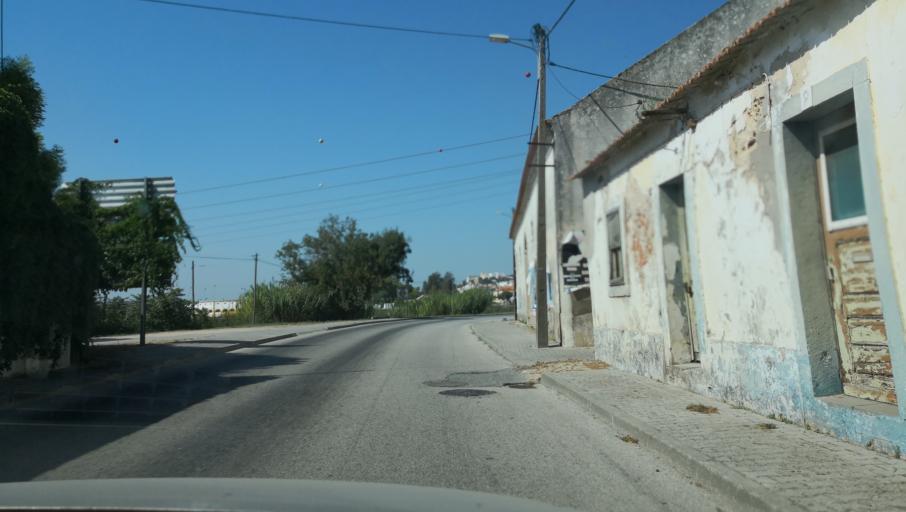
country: PT
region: Setubal
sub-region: Alcacer do Sal
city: Alcacer do Sal
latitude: 38.3689
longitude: -8.4967
